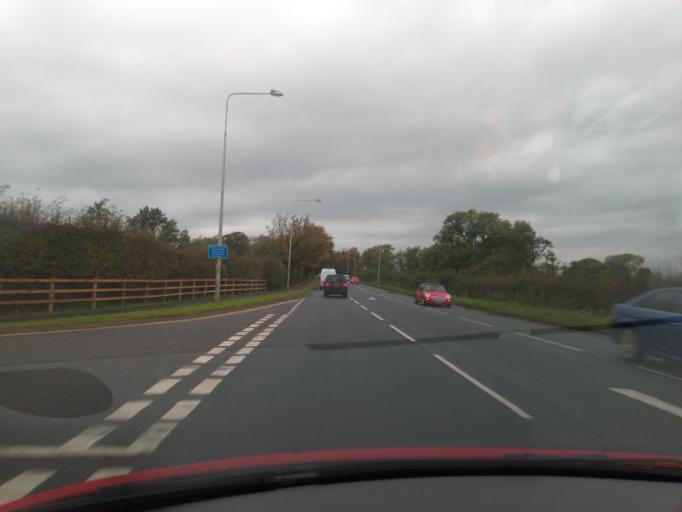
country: GB
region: England
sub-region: Lancashire
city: Catterall
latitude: 53.8442
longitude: -2.7428
